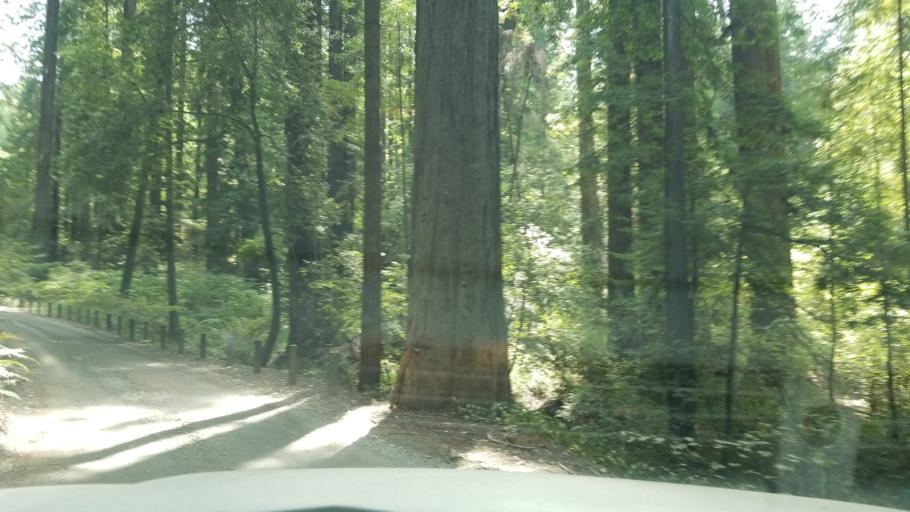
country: US
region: California
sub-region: Humboldt County
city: Redway
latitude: 39.8590
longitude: -123.7174
